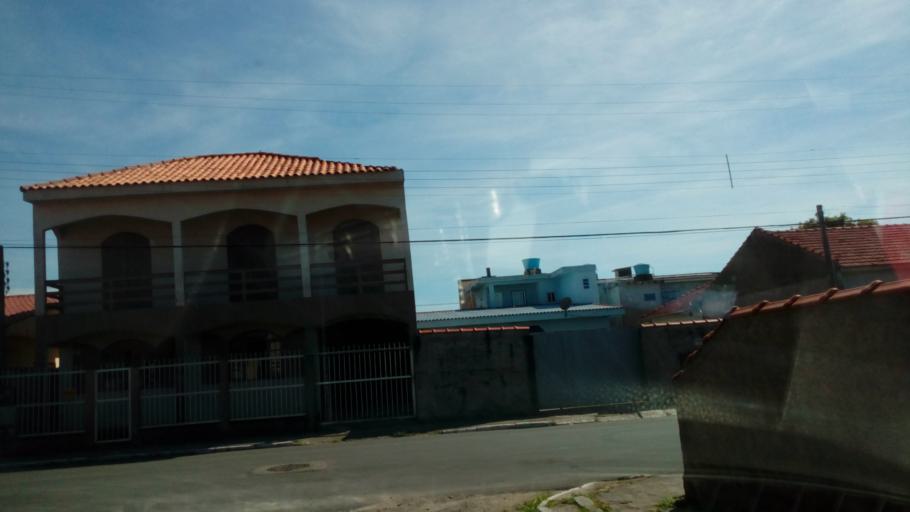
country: BR
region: Santa Catarina
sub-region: Laguna
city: Laguna
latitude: -28.4961
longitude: -48.7770
